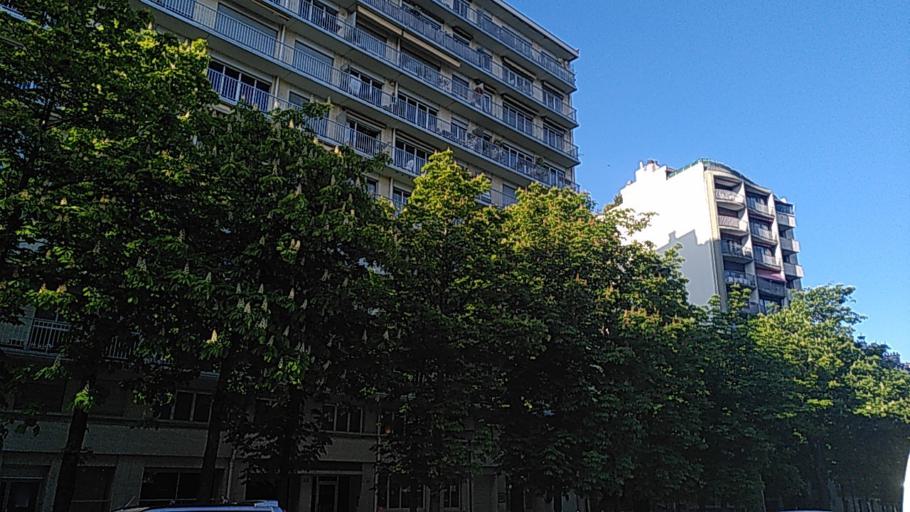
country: FR
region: Ile-de-France
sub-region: Paris
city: Paris
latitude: 48.8349
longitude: 2.3434
